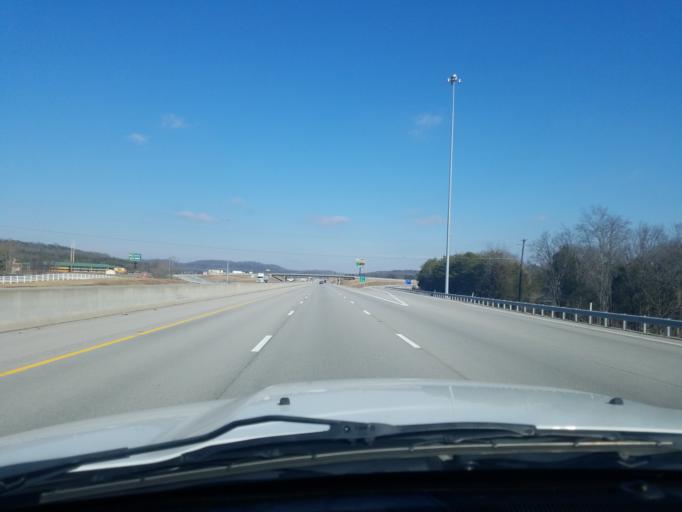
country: US
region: Kentucky
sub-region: Hart County
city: Horse Cave
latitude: 37.1970
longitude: -85.9380
